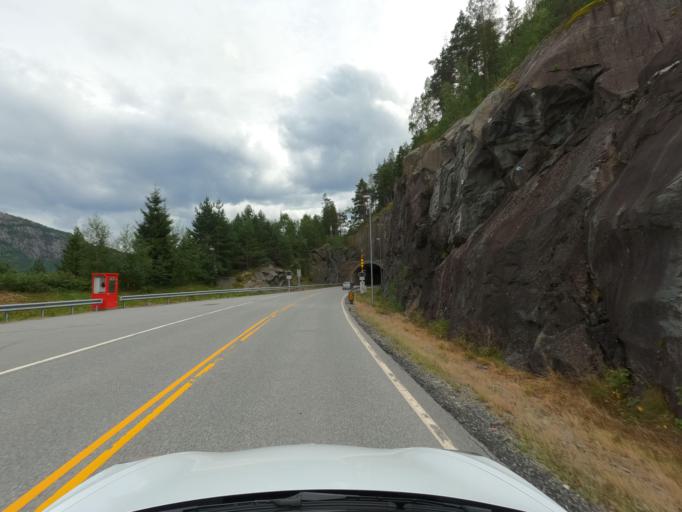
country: NO
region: Telemark
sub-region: Hjartdal
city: Sauland
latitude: 59.8963
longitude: 8.8996
